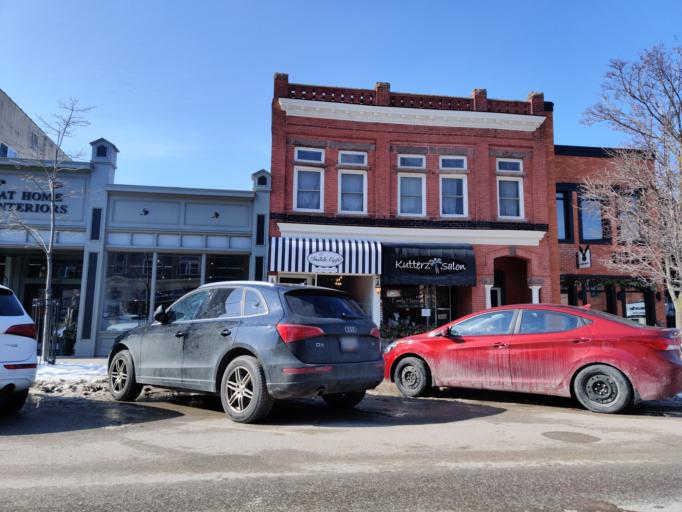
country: CA
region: Ontario
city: Collingwood
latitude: 44.4986
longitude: -80.2166
